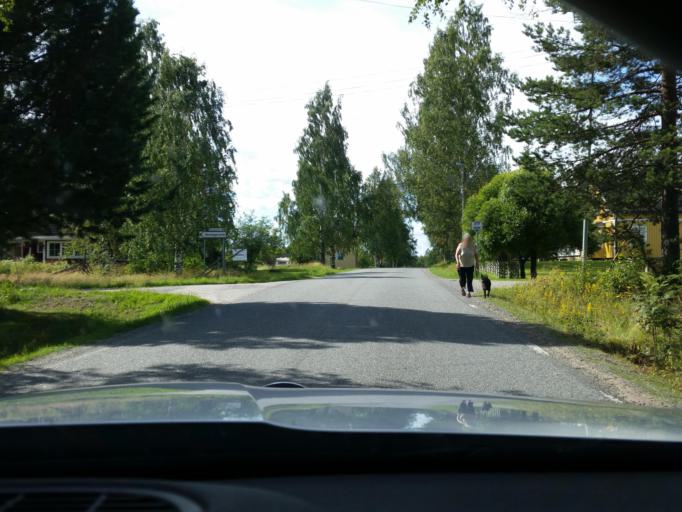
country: SE
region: Norrbotten
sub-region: Pitea Kommun
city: Norrfjarden
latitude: 65.4168
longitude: 21.4767
